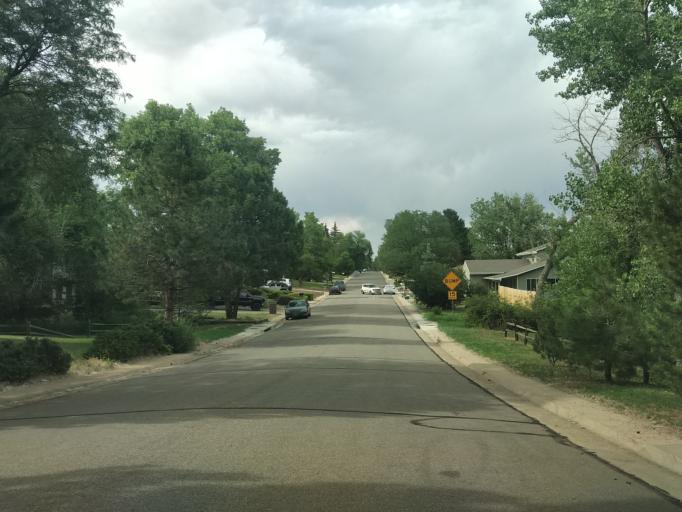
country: US
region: Colorado
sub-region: Jefferson County
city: Lakewood
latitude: 39.6967
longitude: -105.0991
